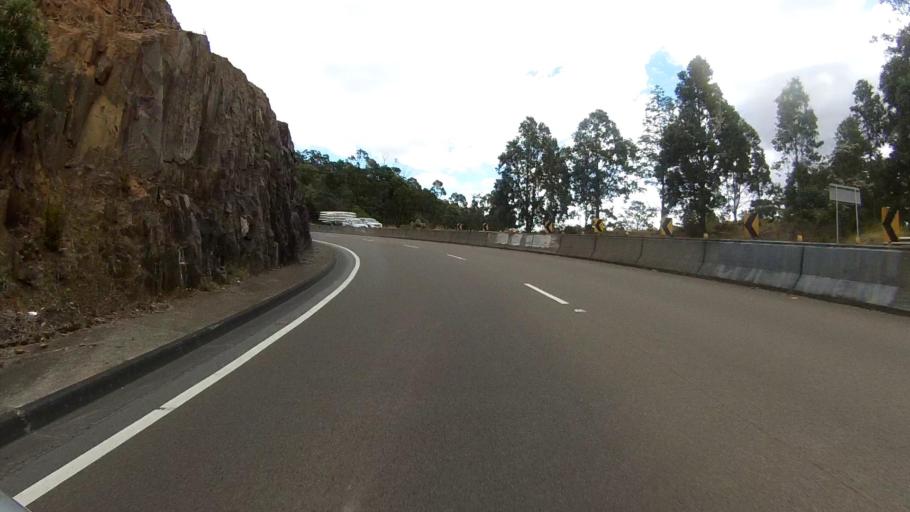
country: AU
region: Tasmania
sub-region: Kingborough
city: Margate
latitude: -42.9813
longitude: 147.1772
